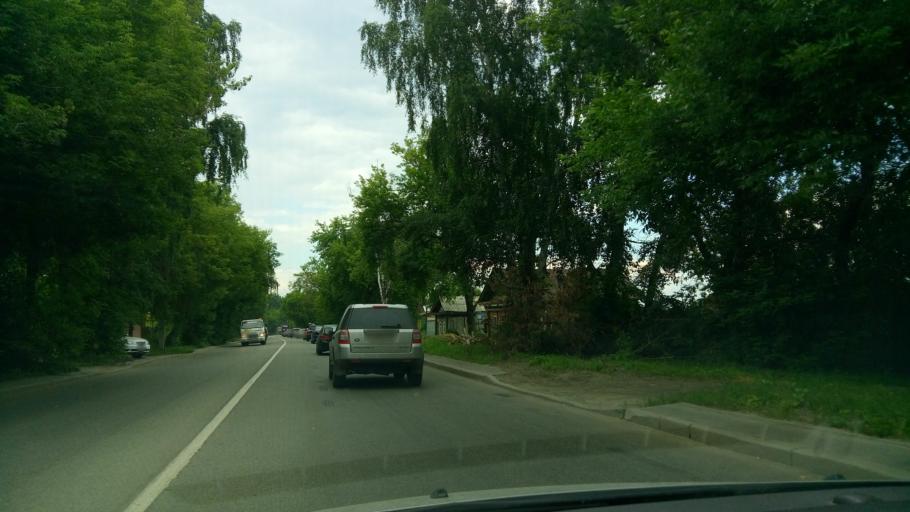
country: RU
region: Sverdlovsk
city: Yekaterinburg
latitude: 56.8789
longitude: 60.6926
